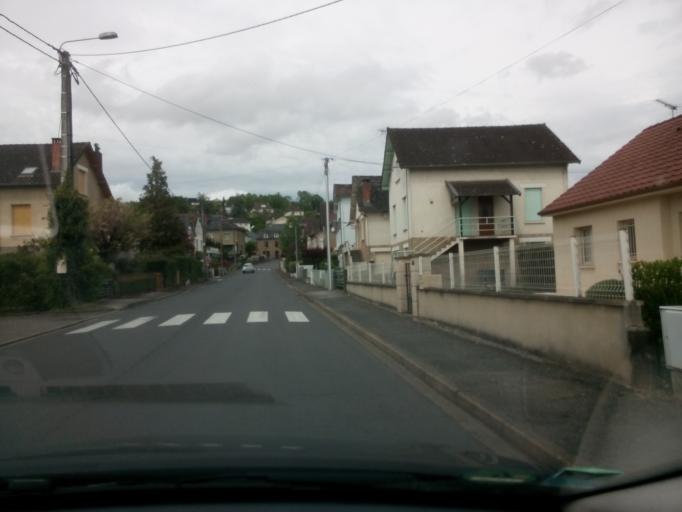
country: FR
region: Limousin
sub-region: Departement de la Correze
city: Objat
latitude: 45.2590
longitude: 1.4084
